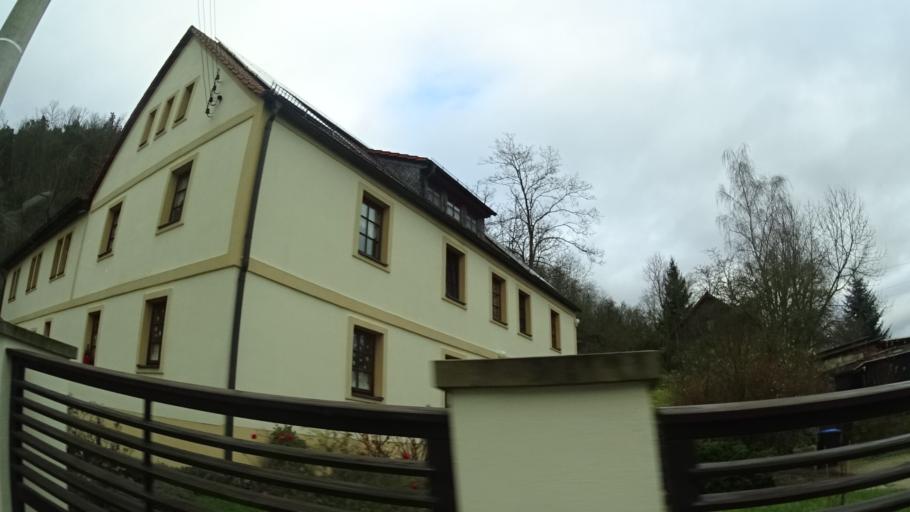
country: DE
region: Thuringia
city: Orlamunde
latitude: 50.7438
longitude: 11.4663
